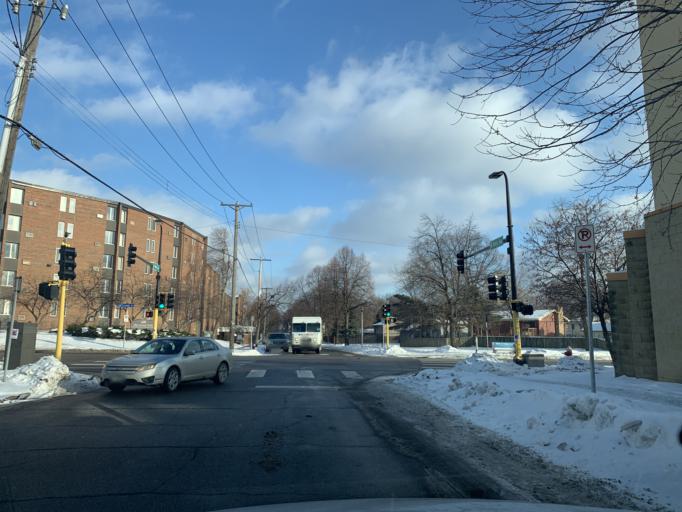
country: US
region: Minnesota
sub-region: Hennepin County
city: Minneapolis
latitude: 44.9974
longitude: -93.2885
